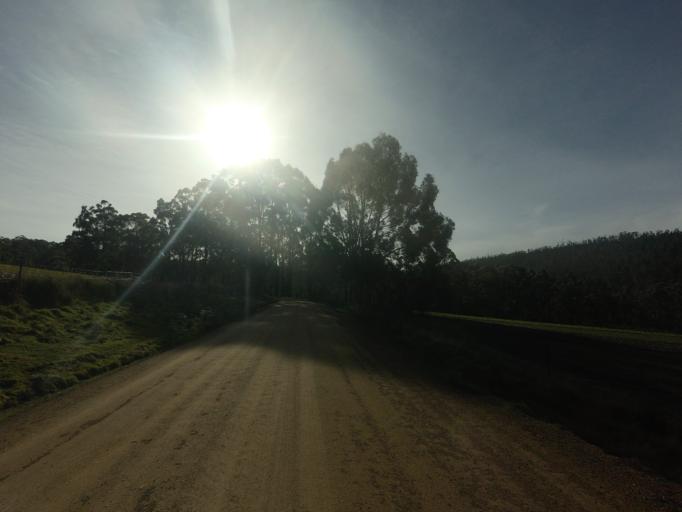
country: AU
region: Tasmania
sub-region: Kingborough
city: Kettering
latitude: -43.0983
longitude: 147.2632
